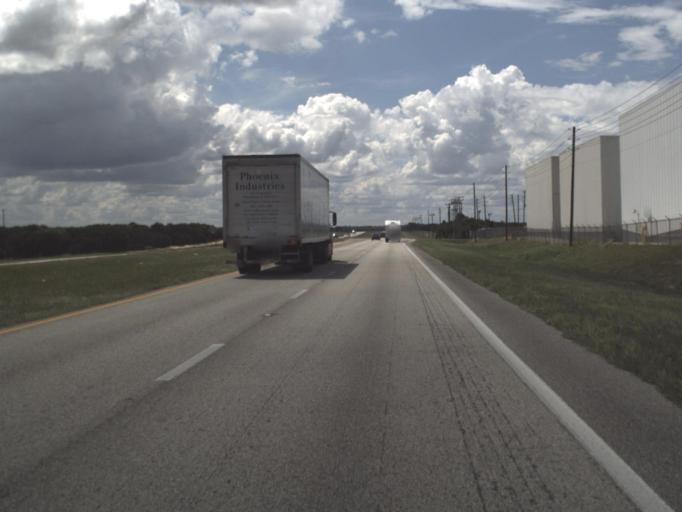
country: US
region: Florida
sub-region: Polk County
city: Babson Park
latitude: 27.8943
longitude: -81.4899
